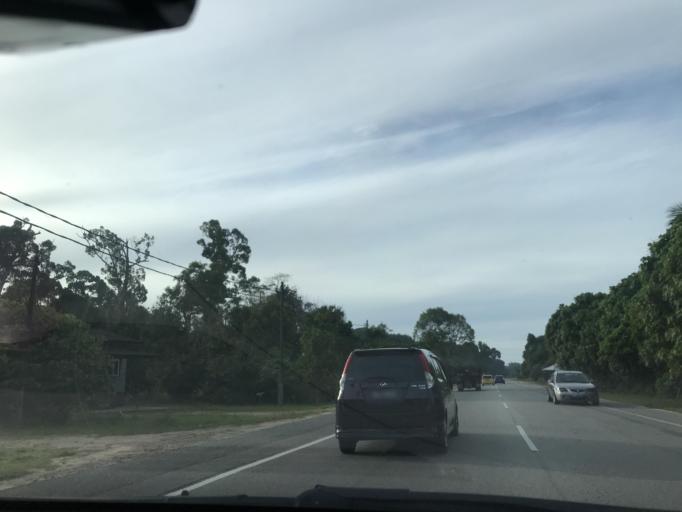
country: MY
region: Kelantan
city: Kampung Lemal
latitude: 6.0048
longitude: 102.1815
